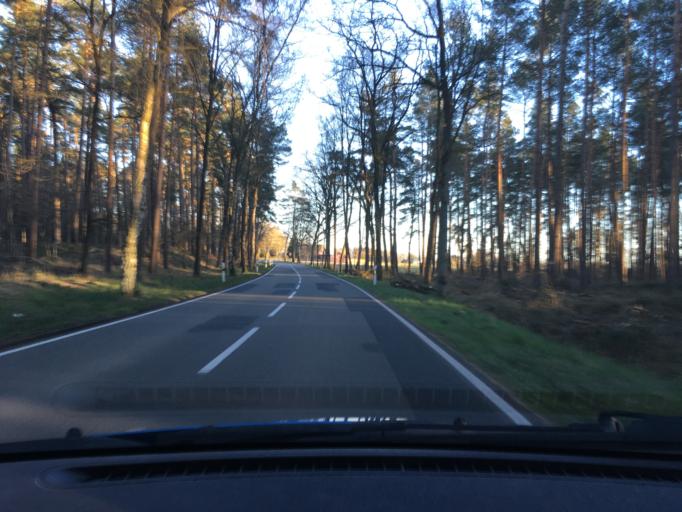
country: DE
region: Lower Saxony
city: Dahlem
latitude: 53.2377
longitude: 10.7523
